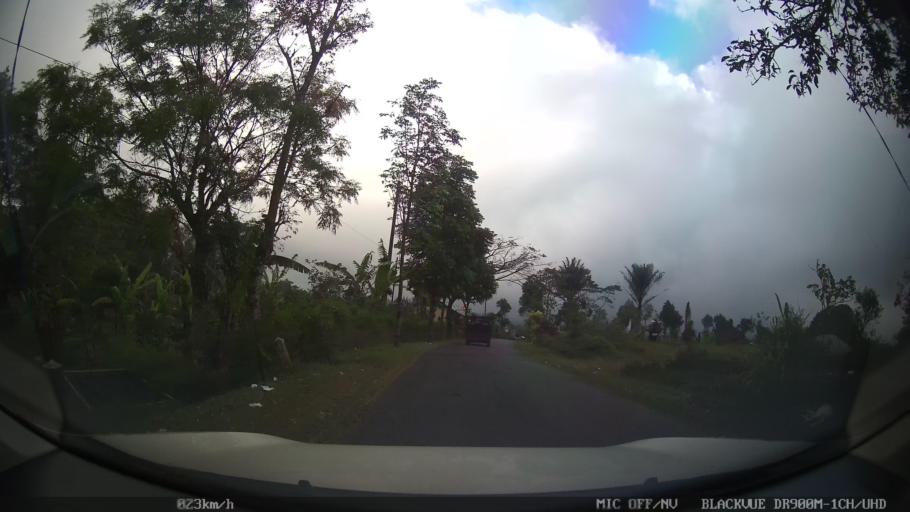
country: ID
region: Bali
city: Banjar Kedisan
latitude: -8.2666
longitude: 115.3311
